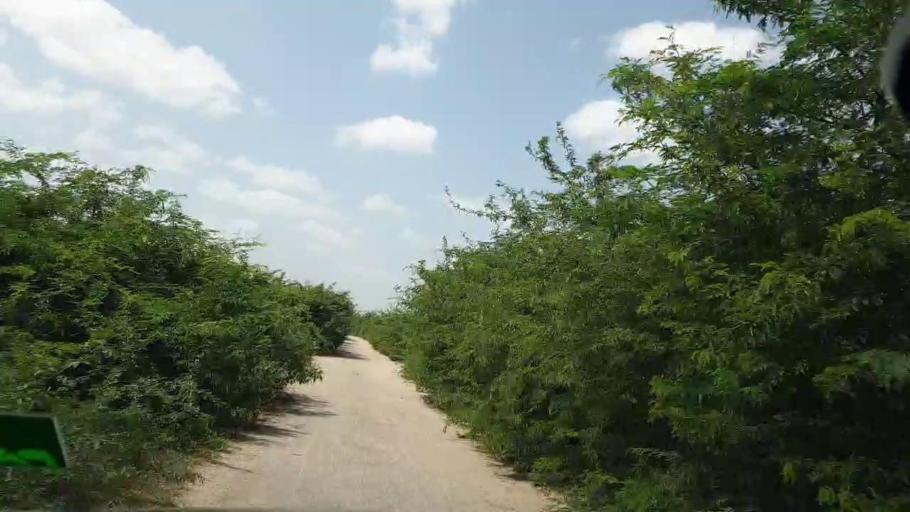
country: PK
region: Sindh
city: Kadhan
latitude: 24.5516
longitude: 69.2045
